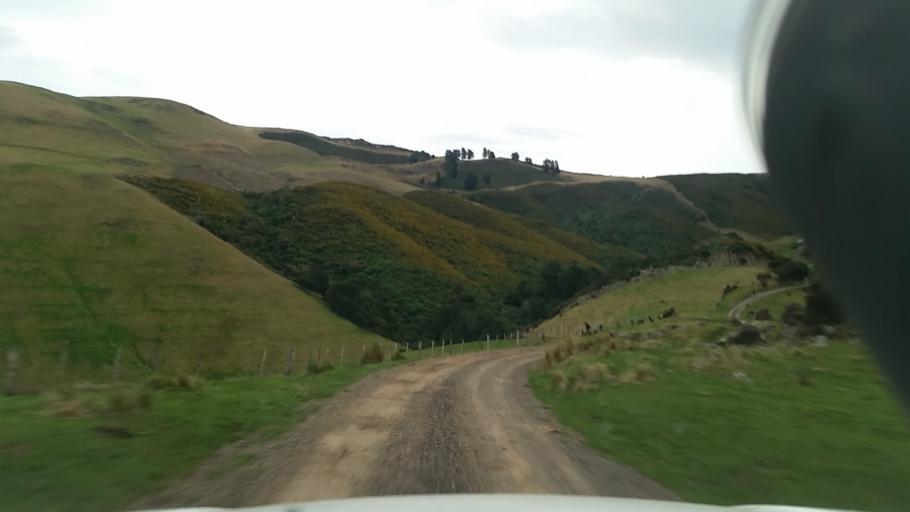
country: NZ
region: Canterbury
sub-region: Christchurch City
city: Christchurch
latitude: -43.8556
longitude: 172.9887
